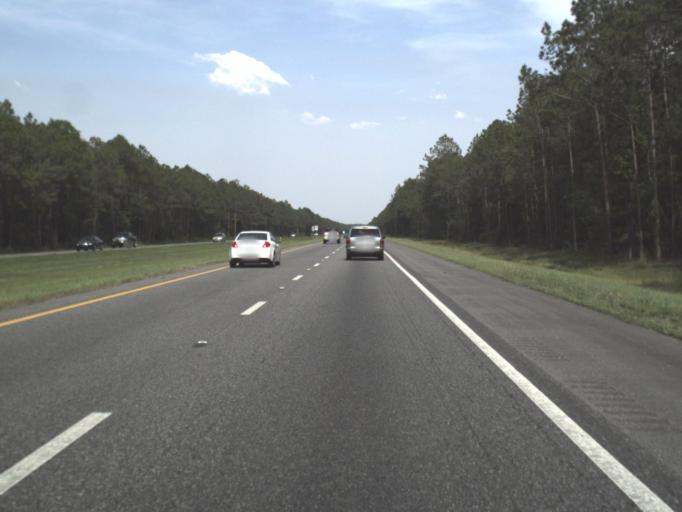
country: US
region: Florida
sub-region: Union County
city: Lake Butler
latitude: 30.2541
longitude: -82.3592
